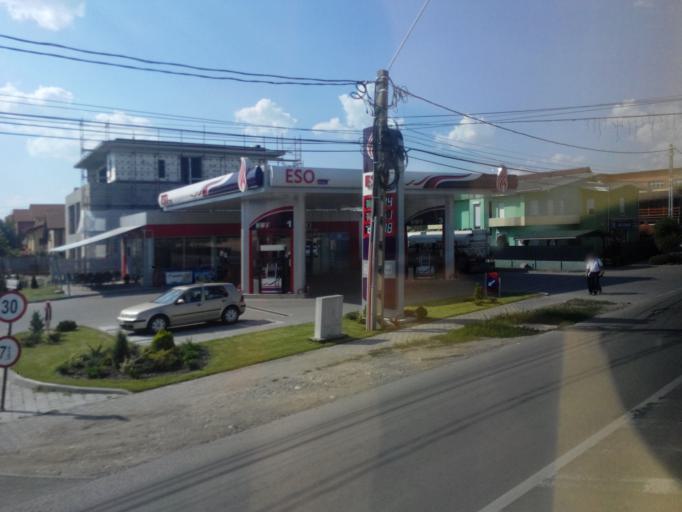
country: RO
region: Timis
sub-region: Comuna Dumbravita
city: Dumbravita
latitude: 45.7882
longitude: 21.2376
